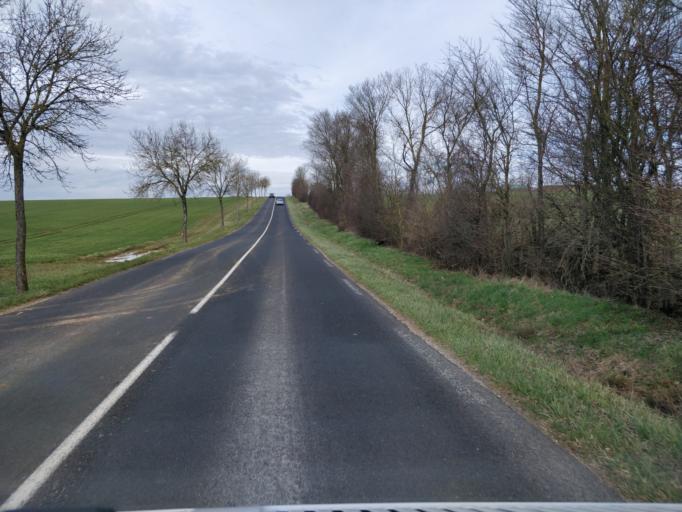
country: FR
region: Lorraine
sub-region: Departement de Meurthe-et-Moselle
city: Montauville
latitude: 48.9049
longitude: 5.9483
